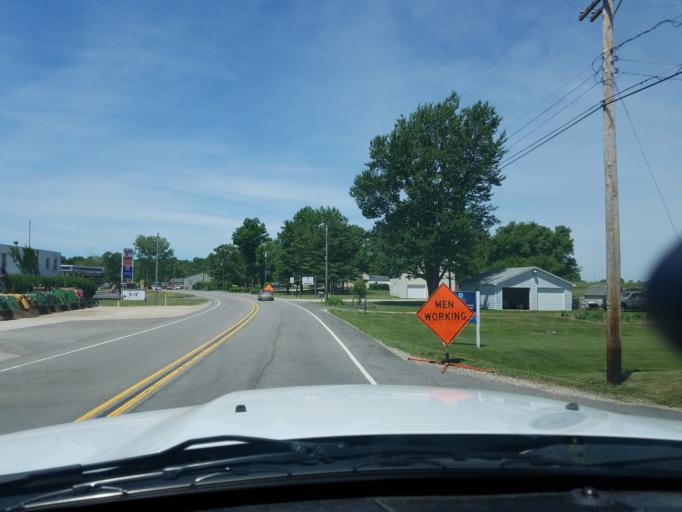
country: US
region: Indiana
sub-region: Delaware County
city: Albany
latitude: 40.3036
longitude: -85.2429
